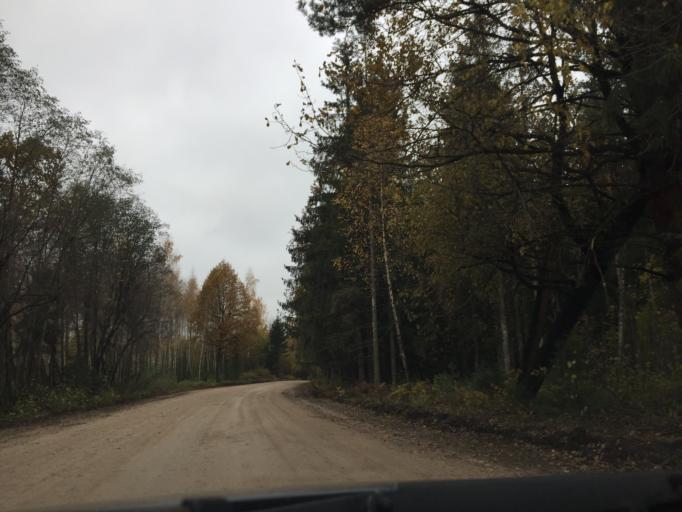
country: LV
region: Sigulda
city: Sigulda
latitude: 57.2737
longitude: 24.8324
